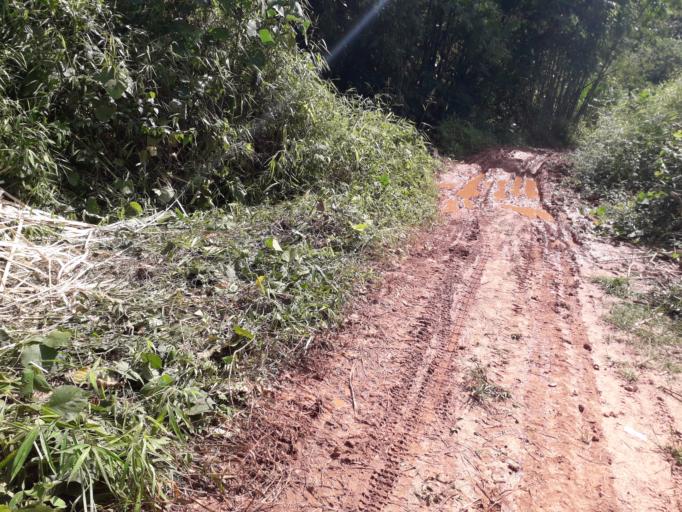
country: CN
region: Yunnan
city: Menglie
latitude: 22.0982
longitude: 101.7372
